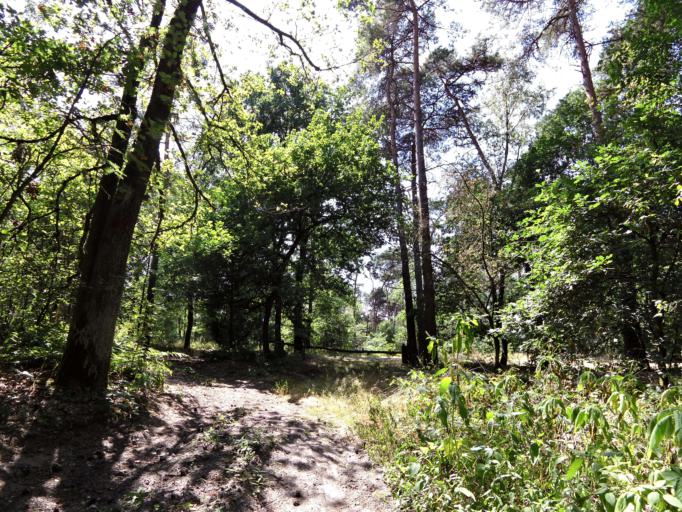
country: NL
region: Limburg
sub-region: Gemeente Leudal
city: Heythuysen
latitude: 51.2082
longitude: 5.8952
